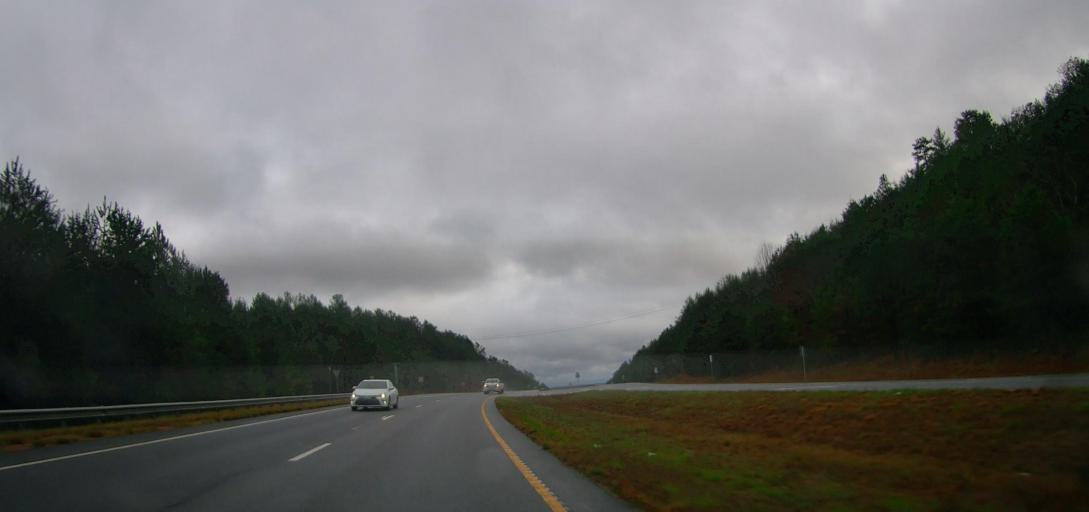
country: US
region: Georgia
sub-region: Habersham County
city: Baldwin
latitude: 34.4761
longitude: -83.5179
